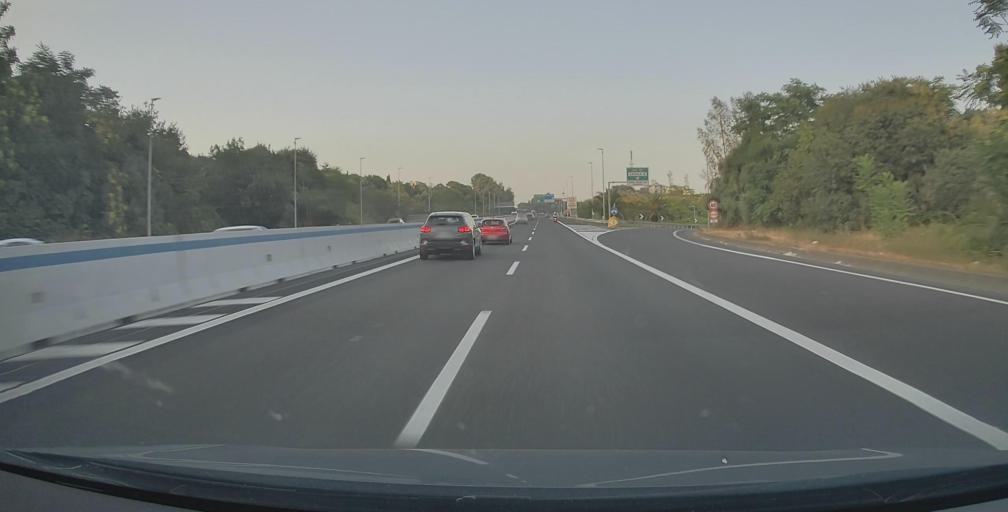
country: IT
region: Sicily
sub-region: Catania
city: Carrubazza-Motta
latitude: 37.5612
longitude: 15.0956
